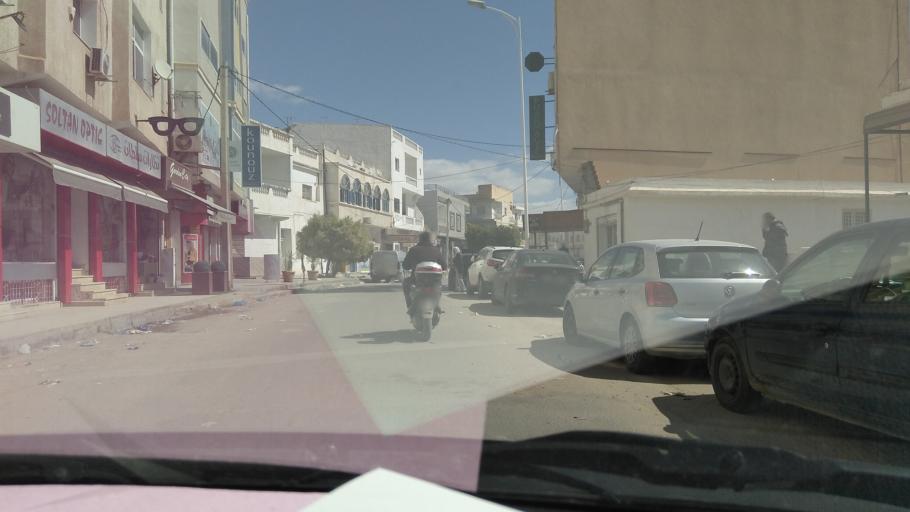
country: TN
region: Al Qayrawan
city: Kairouan
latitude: 35.6709
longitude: 10.1015
